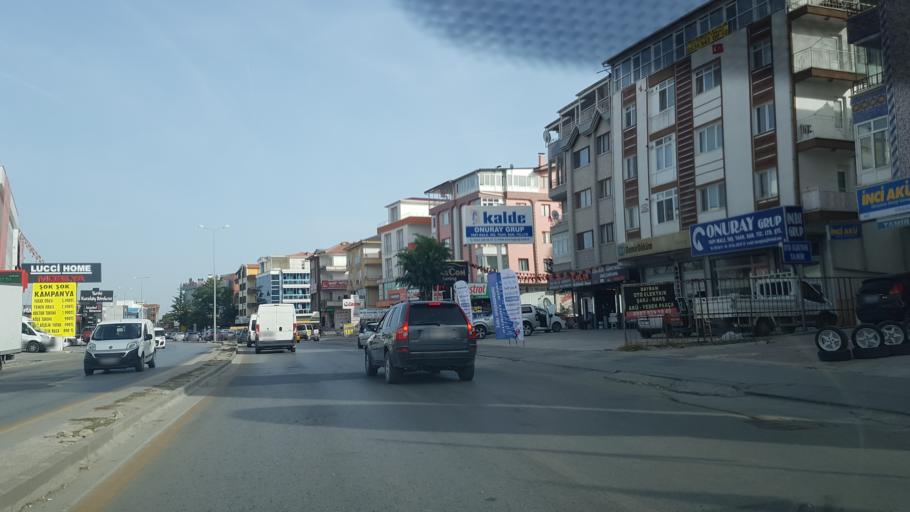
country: TR
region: Ankara
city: Etimesgut
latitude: 39.9529
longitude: 32.6384
